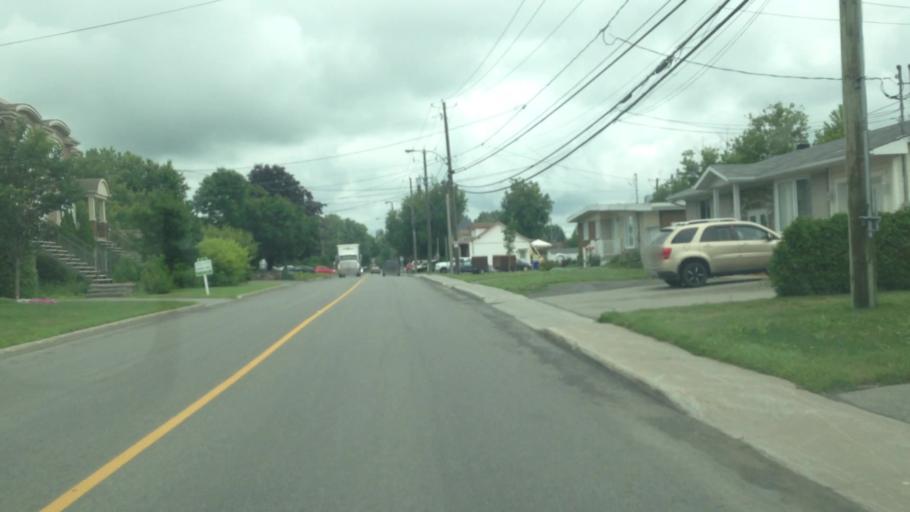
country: CA
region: Quebec
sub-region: Laurentides
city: Blainville
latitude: 45.6983
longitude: -73.9306
